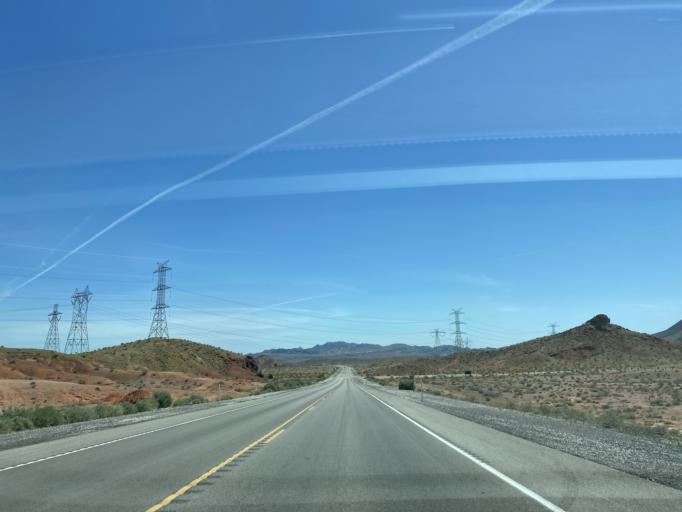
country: US
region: Nevada
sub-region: Clark County
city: Nellis Air Force Base
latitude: 36.1885
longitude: -114.9195
